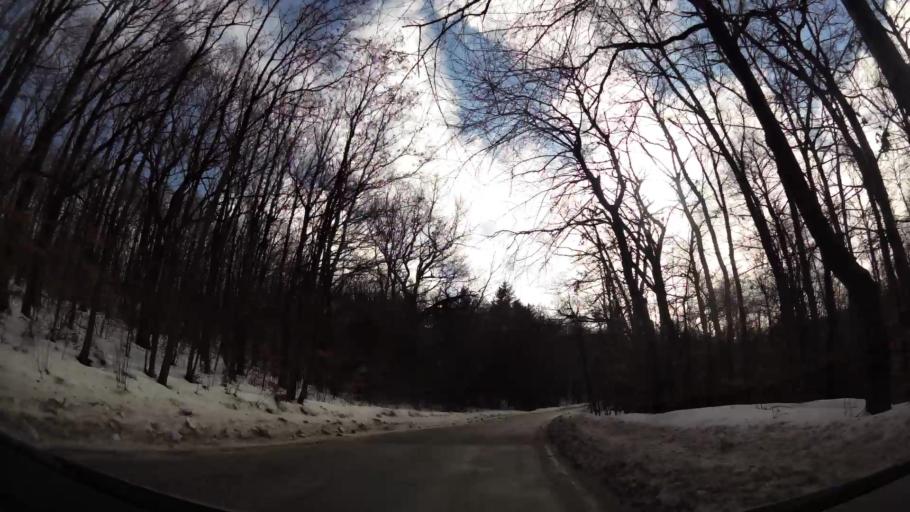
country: BG
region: Sofiya
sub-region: Obshtina Bozhurishte
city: Bozhurishte
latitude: 42.6377
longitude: 23.2211
